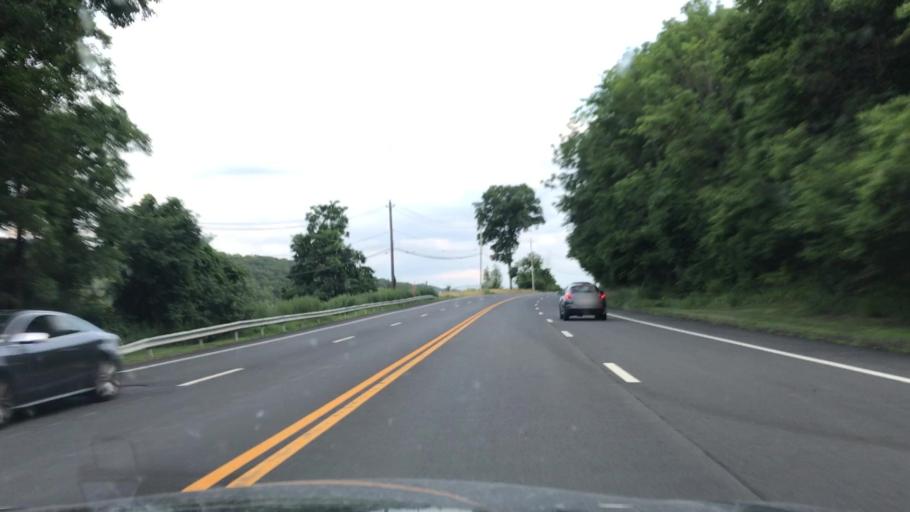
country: US
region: New York
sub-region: Rockland County
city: Sloatsburg
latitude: 41.2139
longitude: -74.1843
